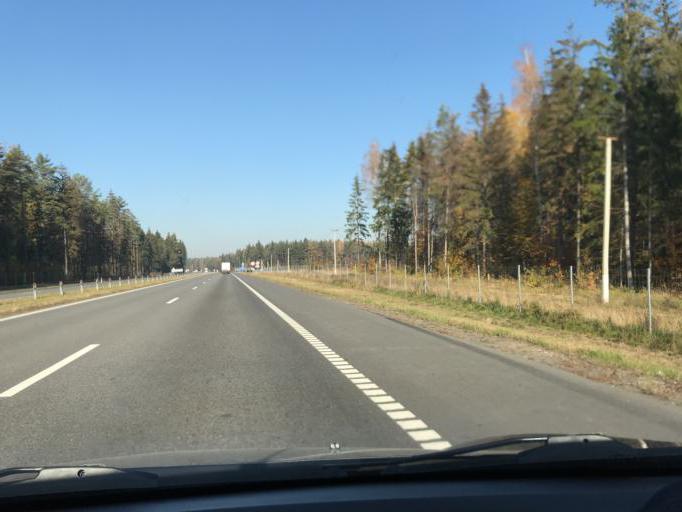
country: BY
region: Mogilev
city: Kirawsk
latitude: 53.2147
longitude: 29.3431
